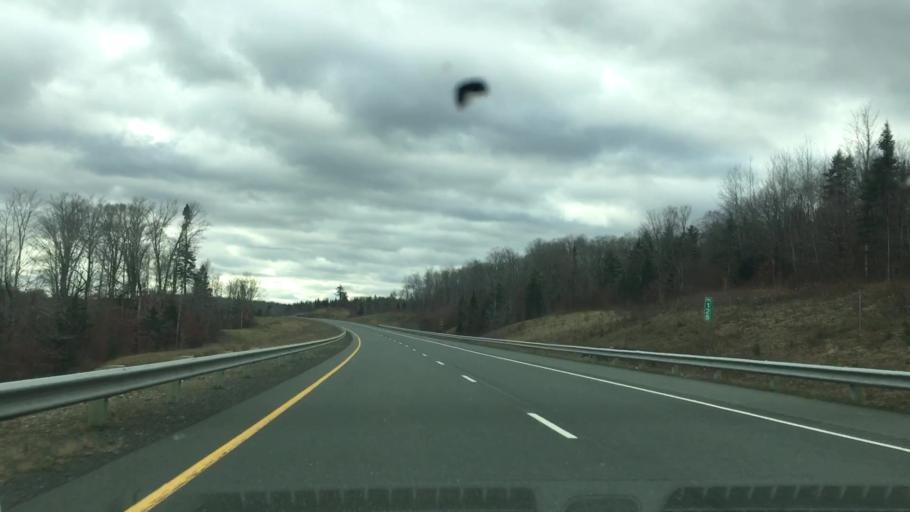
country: US
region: Maine
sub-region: Aroostook County
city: Fort Fairfield
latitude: 46.6470
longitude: -67.7432
